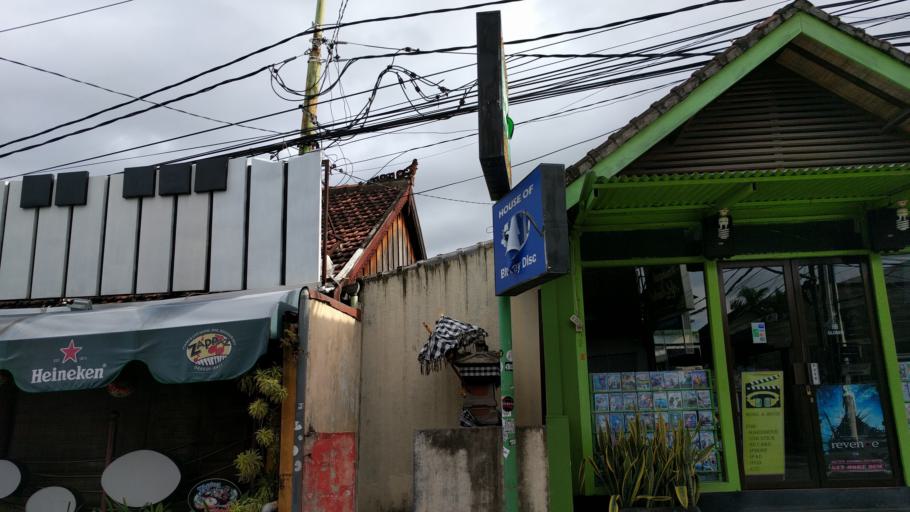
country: ID
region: Bali
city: Kuta
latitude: -8.6841
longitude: 115.1579
